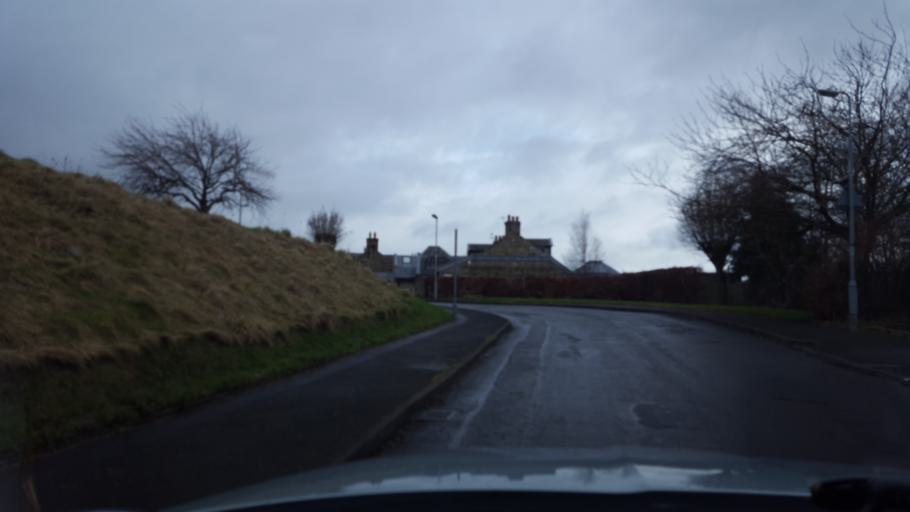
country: GB
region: Scotland
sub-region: Edinburgh
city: Currie
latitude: 55.8962
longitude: -3.3079
